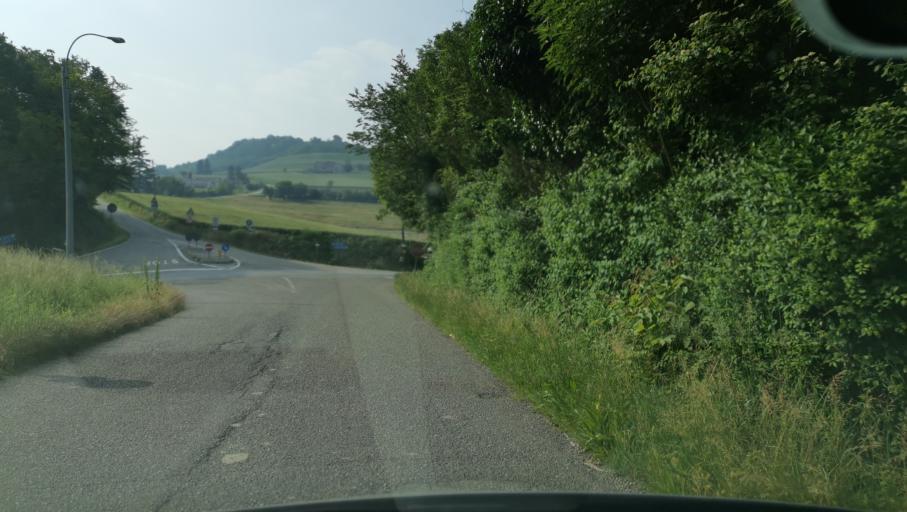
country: IT
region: Piedmont
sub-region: Provincia di Alessandria
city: Castelletto Merli
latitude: 45.0631
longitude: 8.2397
